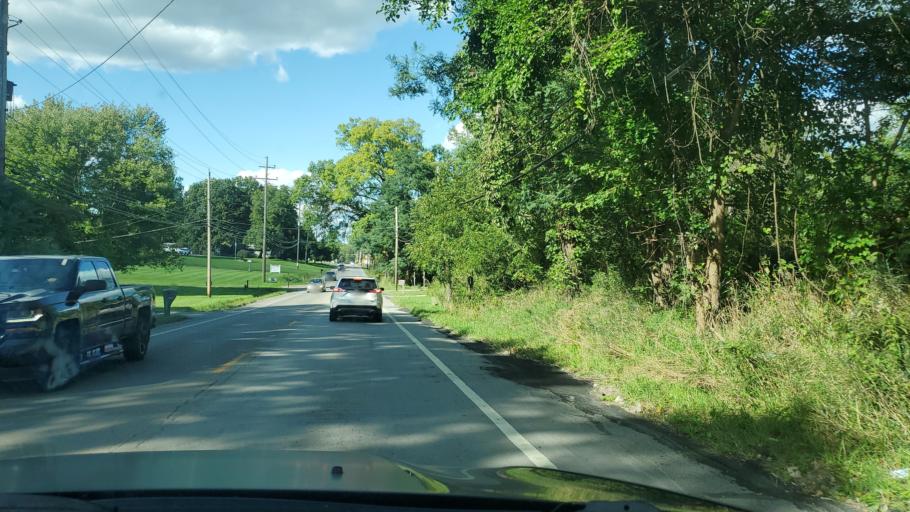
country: US
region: Ohio
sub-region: Trumbull County
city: Mineral Ridge
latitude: 41.1544
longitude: -80.7688
